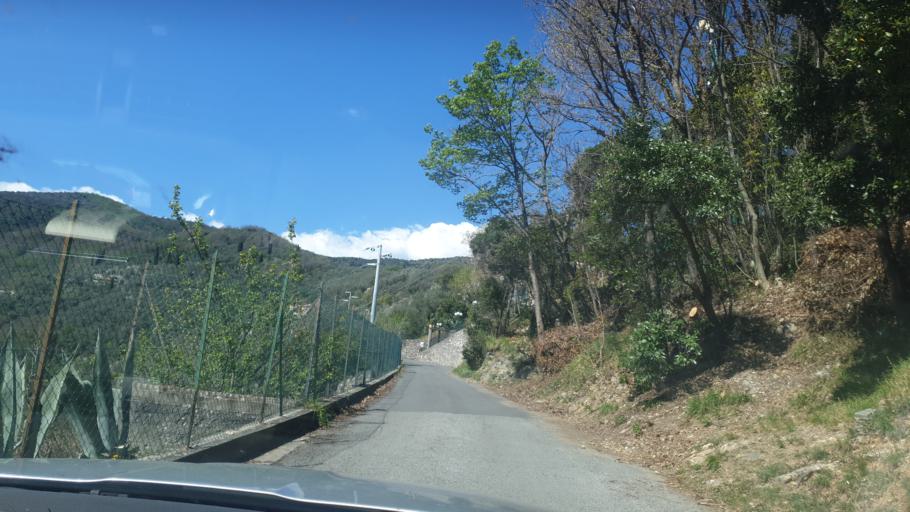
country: IT
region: Liguria
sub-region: Provincia di Genova
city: Avegno
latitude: 44.3788
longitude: 9.1487
